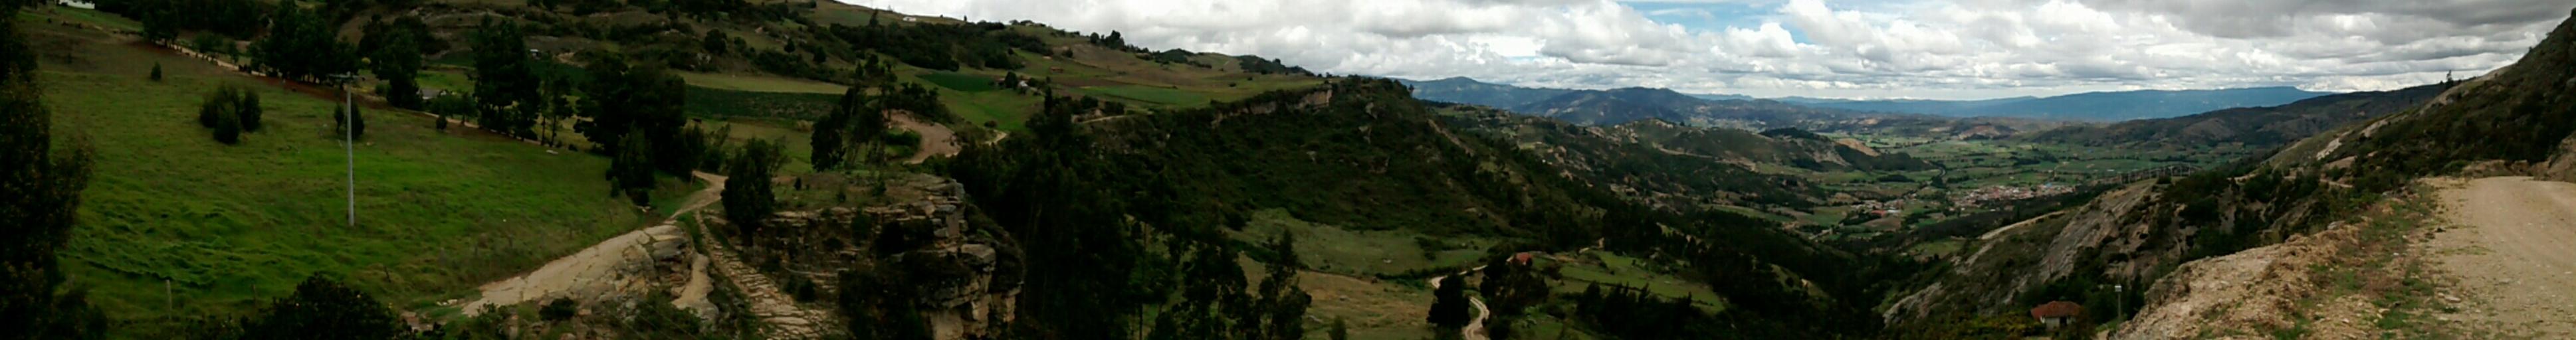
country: CO
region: Boyaca
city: Cucaita
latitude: 5.5383
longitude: -73.4319
